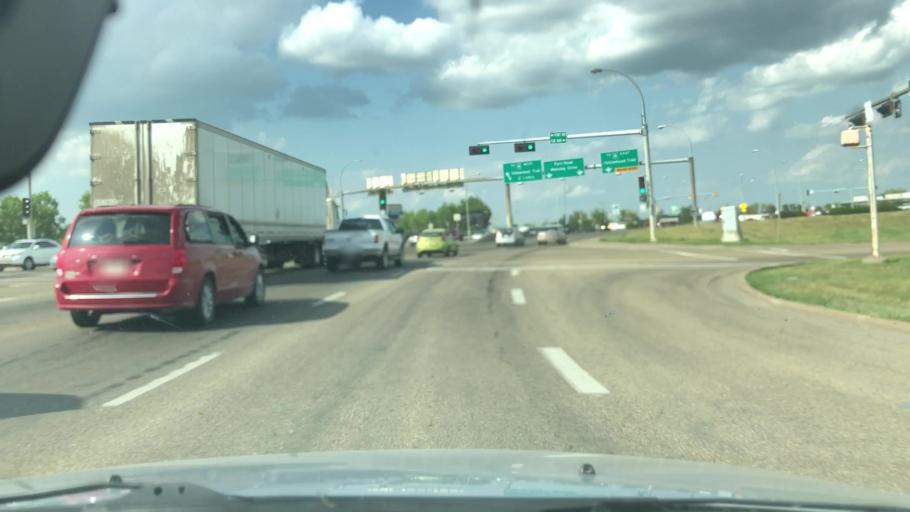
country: CA
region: Alberta
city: Edmonton
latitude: 53.5788
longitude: -113.4543
